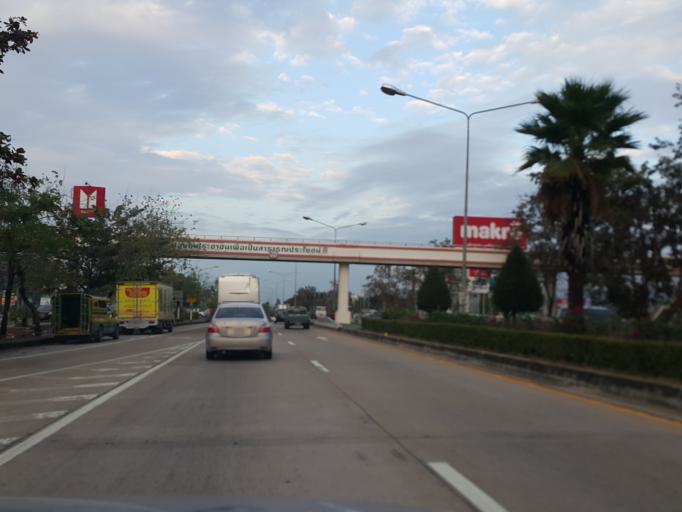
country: TH
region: Lampang
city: Lampang
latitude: 18.2753
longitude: 99.4824
